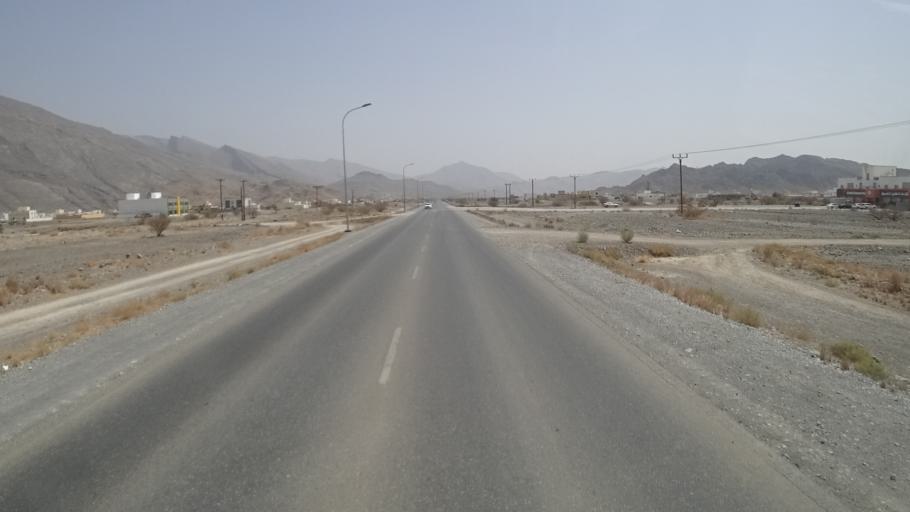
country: OM
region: Muhafazat ad Dakhiliyah
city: Nizwa
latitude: 23.0301
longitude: 57.4921
